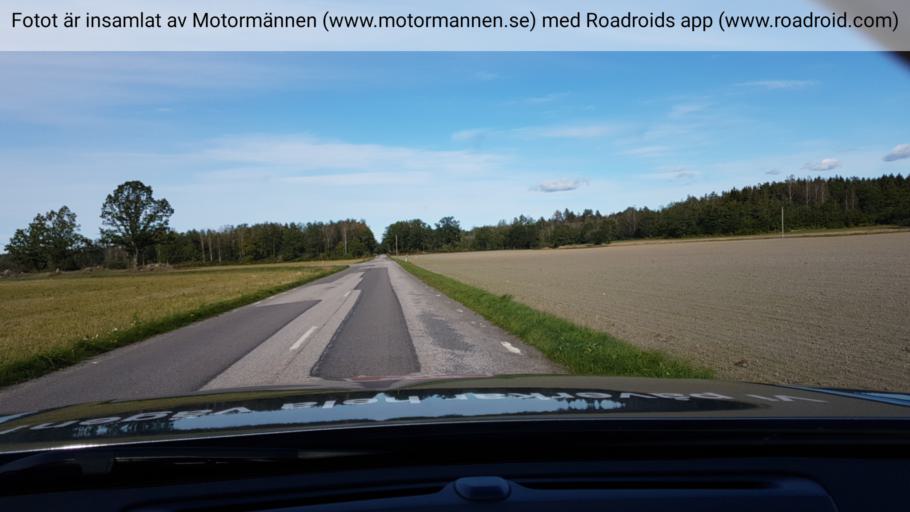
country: SE
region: Kalmar
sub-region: Vasterviks Kommun
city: Forserum
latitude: 58.0371
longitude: 16.5956
